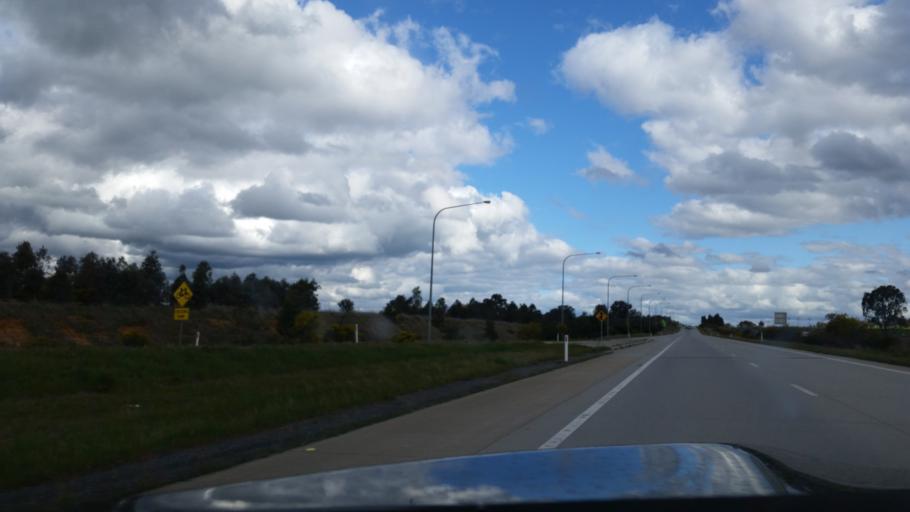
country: AU
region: New South Wales
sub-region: Greater Hume Shire
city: Jindera
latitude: -35.9354
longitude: 147.0031
